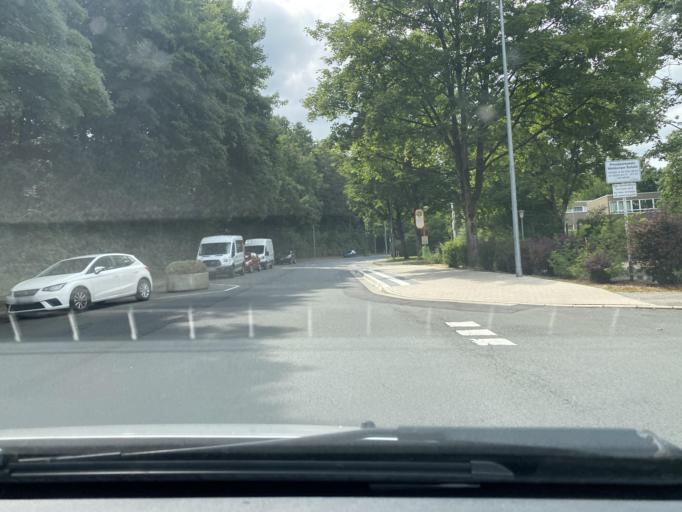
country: DE
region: North Rhine-Westphalia
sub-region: Regierungsbezirk Arnsberg
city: Luedenscheid
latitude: 51.2333
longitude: 7.6200
